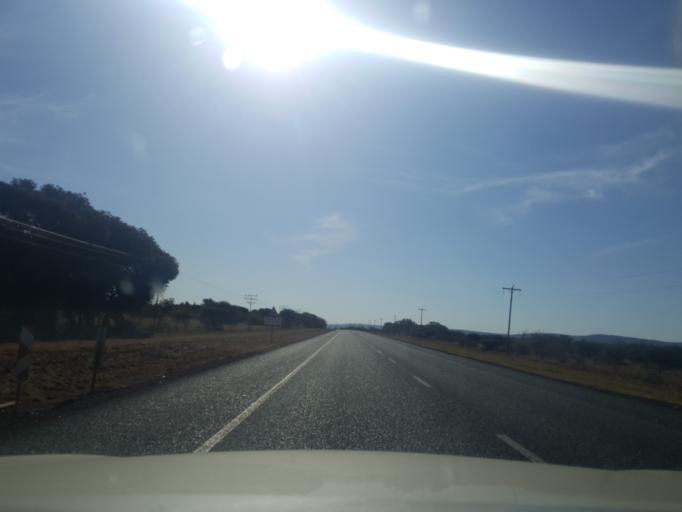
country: ZA
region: North-West
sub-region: Ngaka Modiri Molema District Municipality
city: Zeerust
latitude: -25.5503
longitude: 26.2074
